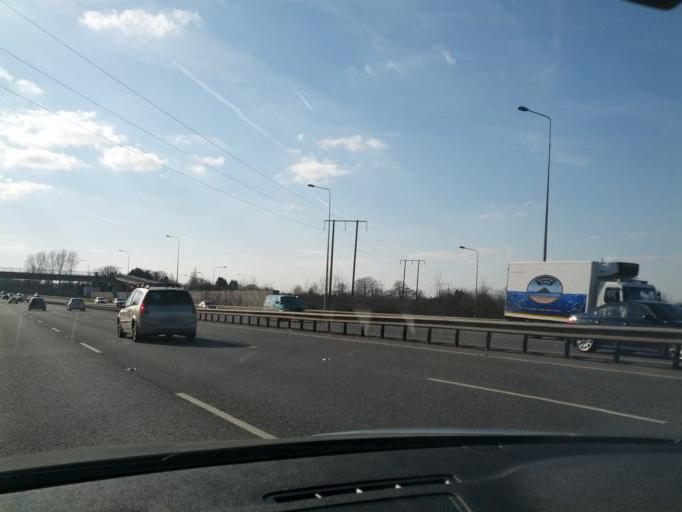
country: IE
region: Leinster
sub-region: Kildare
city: Kill
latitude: 53.2509
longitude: -6.5845
